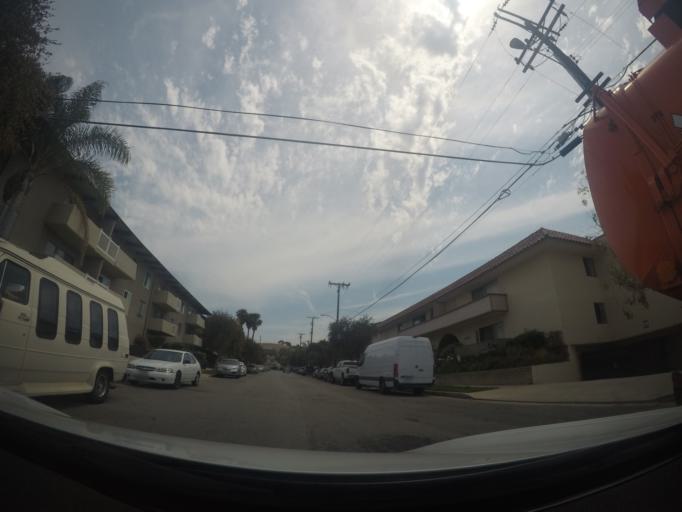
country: US
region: California
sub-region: Los Angeles County
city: Rolling Hills Estates
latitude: 33.8079
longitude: -118.3528
